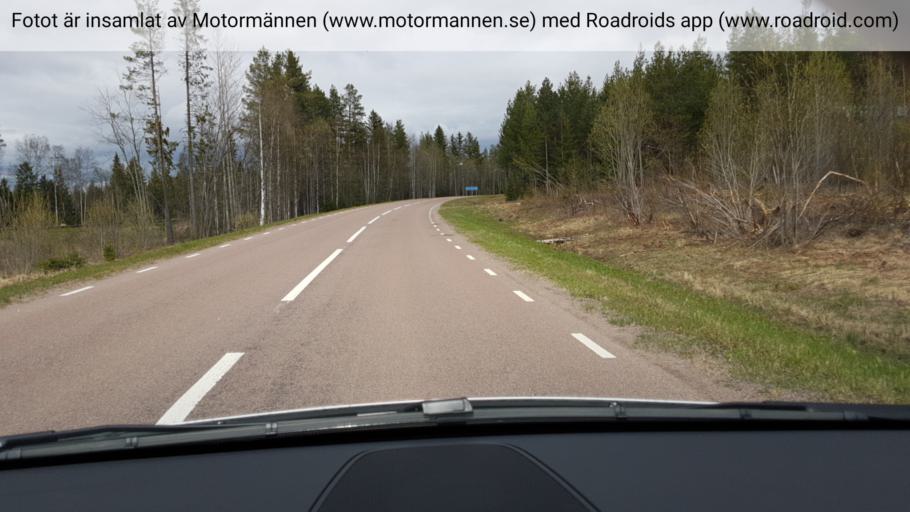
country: SE
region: Jaemtland
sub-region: Braecke Kommun
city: Braecke
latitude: 62.9492
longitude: 15.7286
